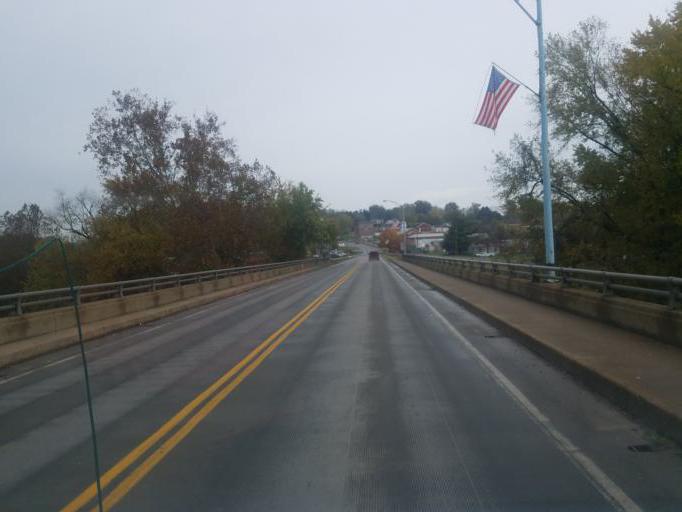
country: US
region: Ohio
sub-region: Washington County
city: Beverly
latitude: 39.5443
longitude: -81.6410
